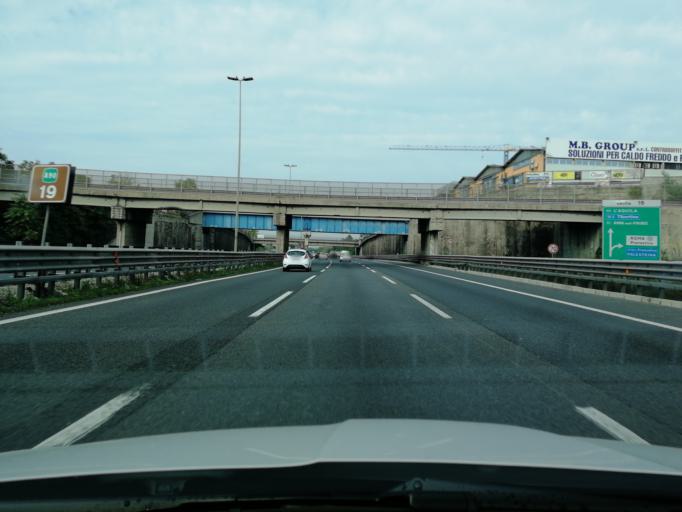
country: IT
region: Latium
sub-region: Citta metropolitana di Roma Capitale
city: Setteville
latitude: 41.8908
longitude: 12.6150
